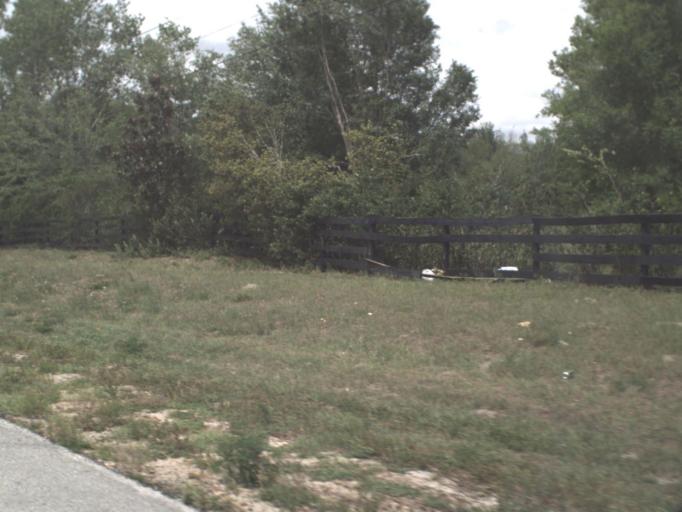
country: US
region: Florida
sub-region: Lake County
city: Mount Dora
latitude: 28.8514
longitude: -81.5913
